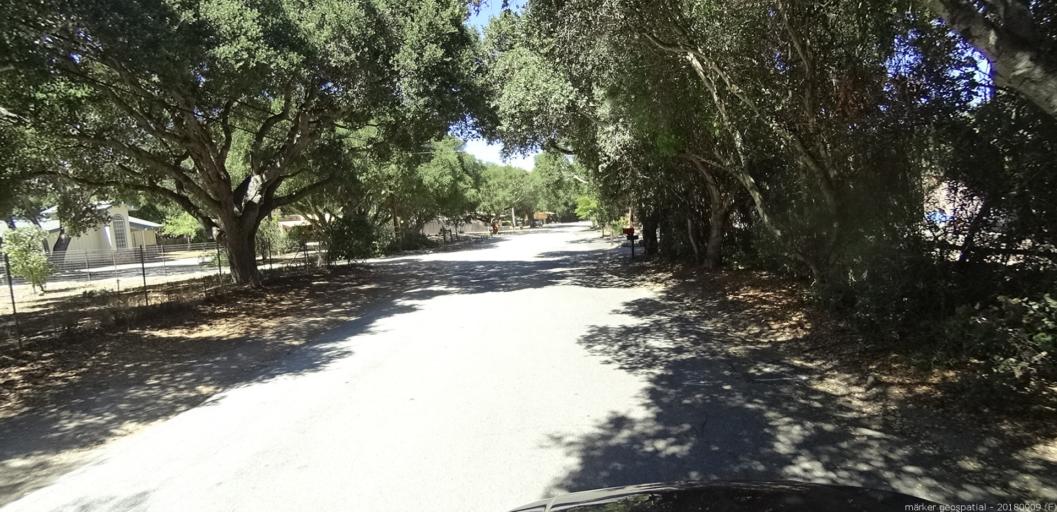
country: US
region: California
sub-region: Monterey County
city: Carmel Valley Village
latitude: 36.5746
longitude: -121.7189
